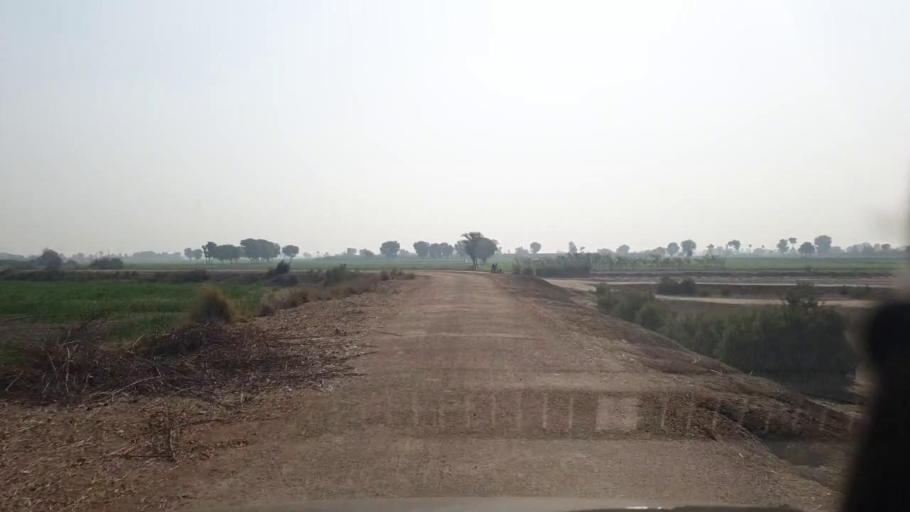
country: PK
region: Sindh
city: Shahdadpur
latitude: 26.0406
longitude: 68.4921
